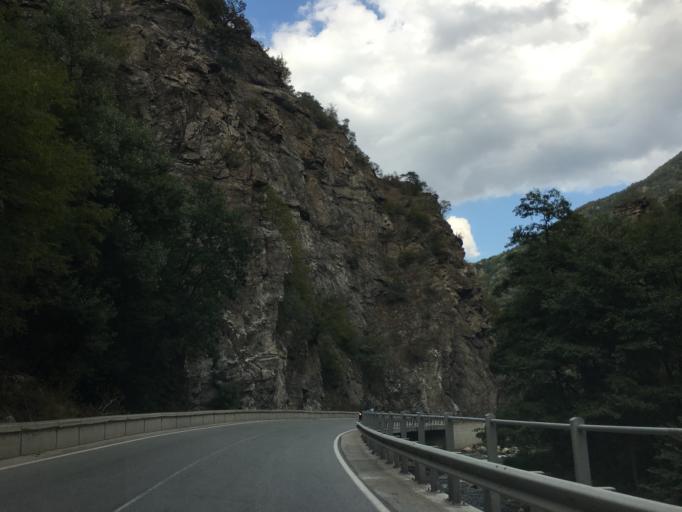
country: BG
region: Pazardzhik
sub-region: Obshtina Septemvri
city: Septemvri
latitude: 42.1103
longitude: 24.1089
